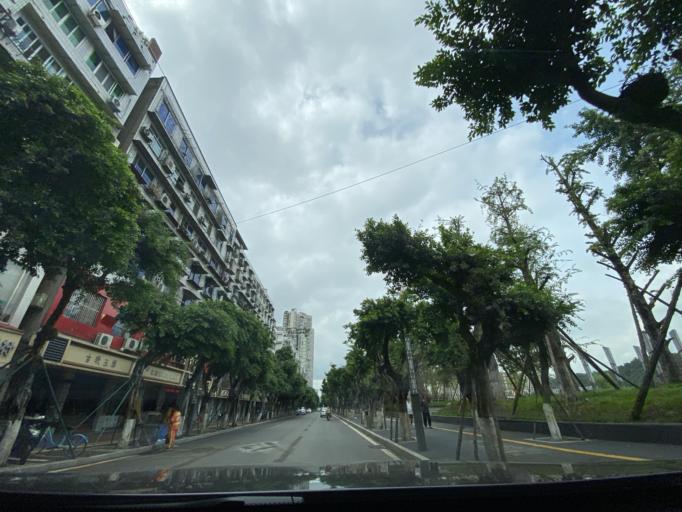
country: CN
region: Sichuan
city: Jiancheng
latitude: 30.3952
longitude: 104.5528
